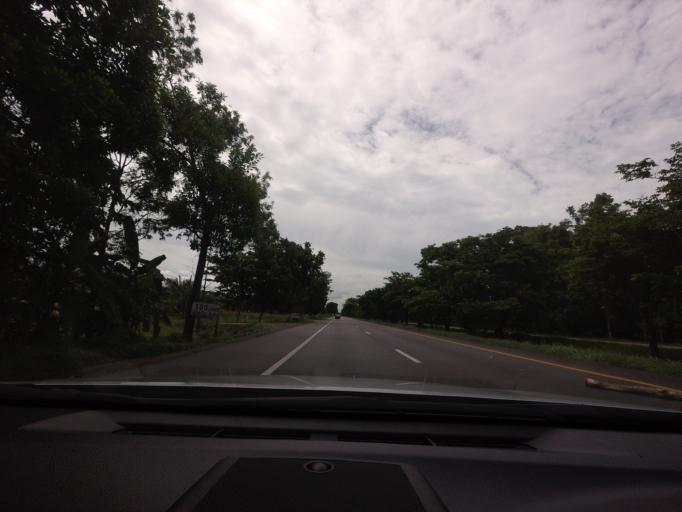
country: TH
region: Chumphon
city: Lamae
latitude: 9.7308
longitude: 99.1027
